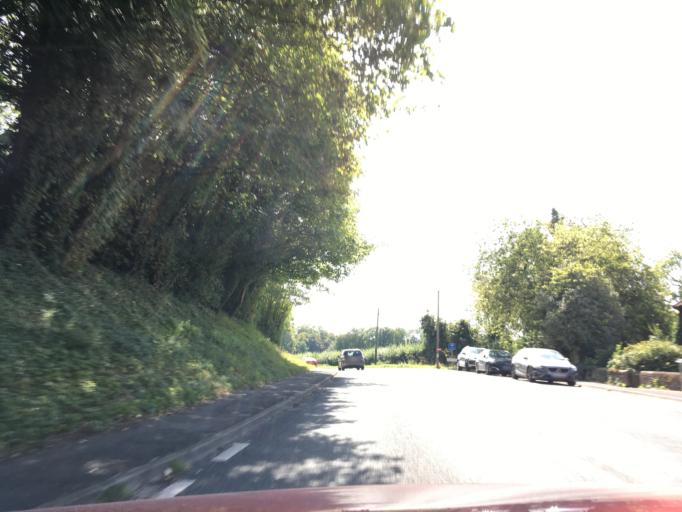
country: GB
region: England
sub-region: Hampshire
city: Compton
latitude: 51.0292
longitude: -1.3150
